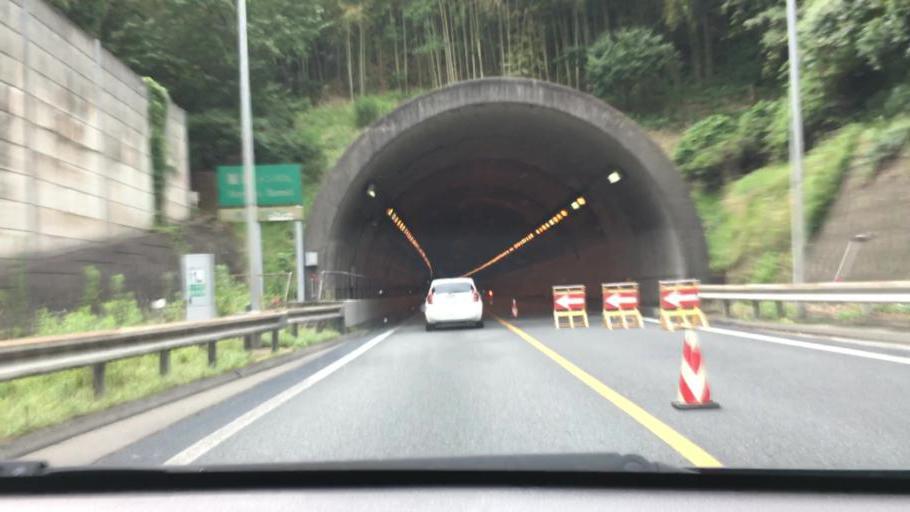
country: JP
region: Yamaguchi
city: Tokuyama
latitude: 34.0890
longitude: 131.7759
